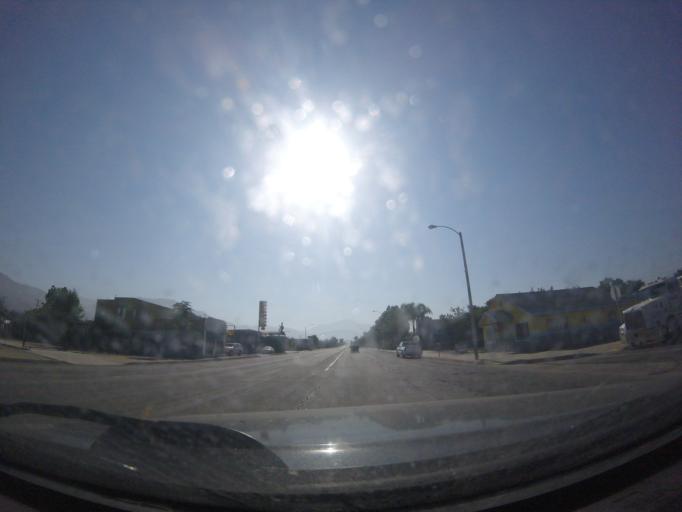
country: US
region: California
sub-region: San Bernardino County
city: Highland
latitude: 34.1213
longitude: -117.2249
